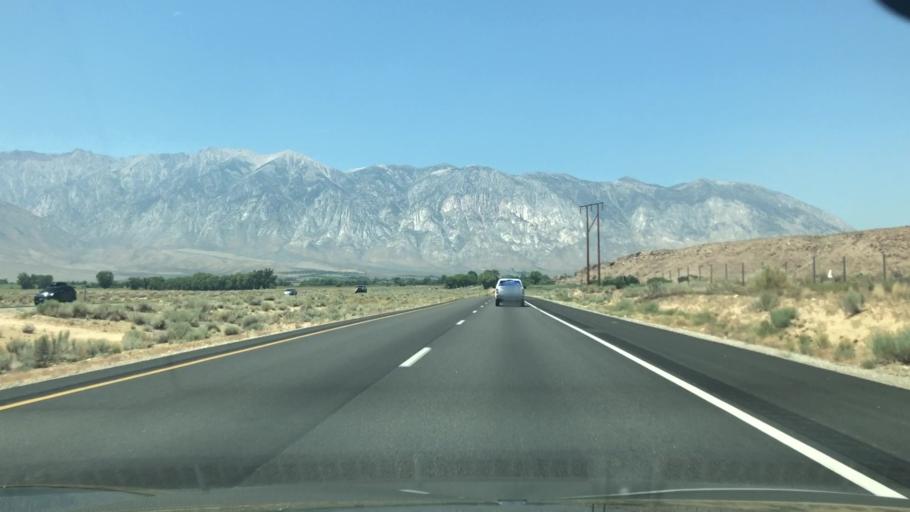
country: US
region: California
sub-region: Inyo County
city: West Bishop
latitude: 37.3995
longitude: -118.5263
